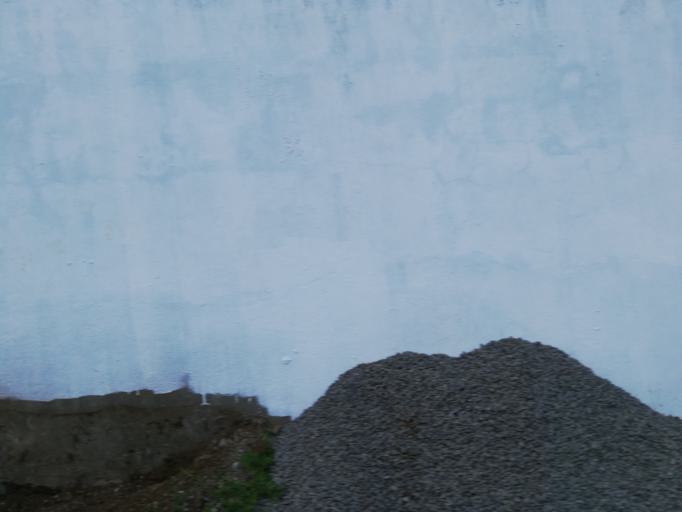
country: MU
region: Plaines Wilhems
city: Ebene
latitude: -20.2325
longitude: 57.4600
